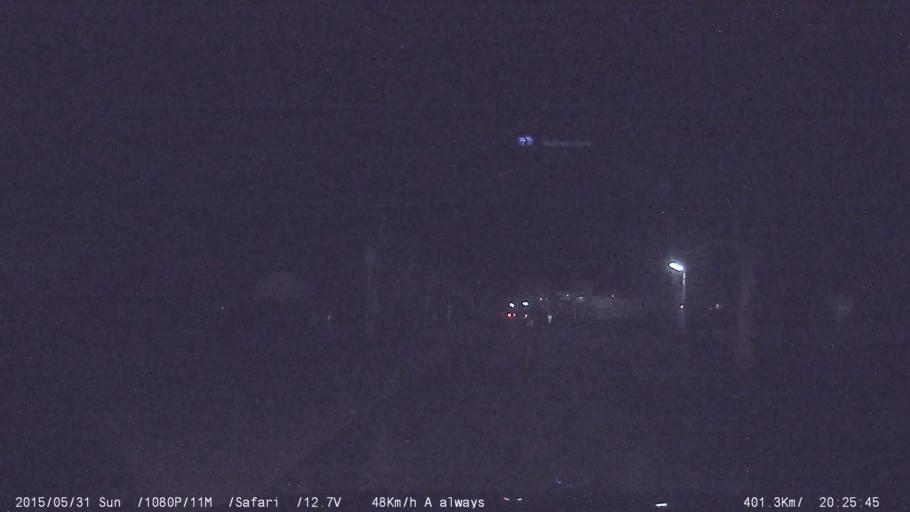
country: IN
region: Karnataka
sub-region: Mandya
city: Malavalli
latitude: 12.4309
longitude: 77.2310
